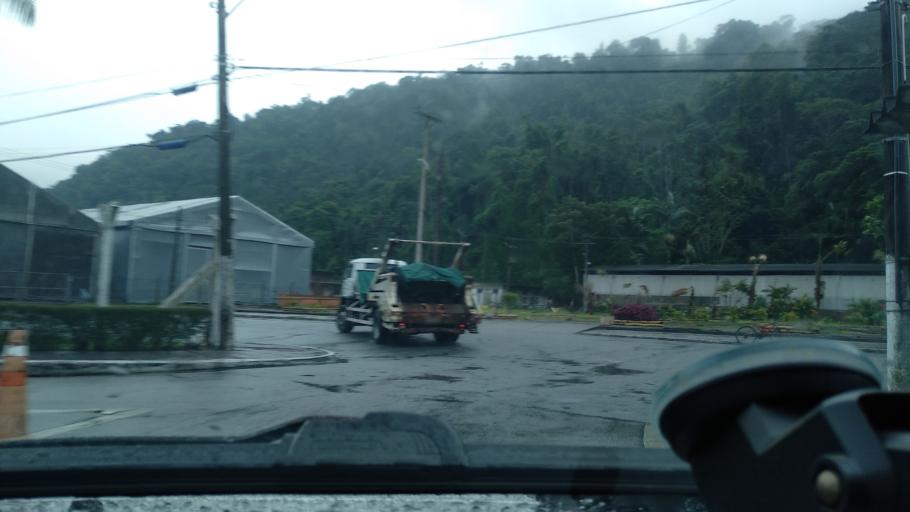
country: BR
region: Rio de Janeiro
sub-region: Angra Dos Reis
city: Angra dos Reis
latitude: -23.0296
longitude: -44.5440
